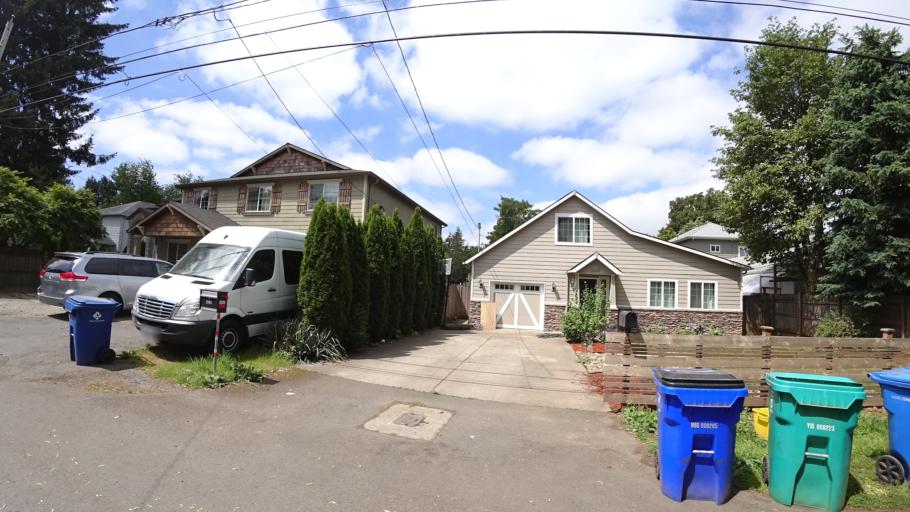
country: US
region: Oregon
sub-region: Multnomah County
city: Gresham
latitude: 45.5031
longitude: -122.4912
